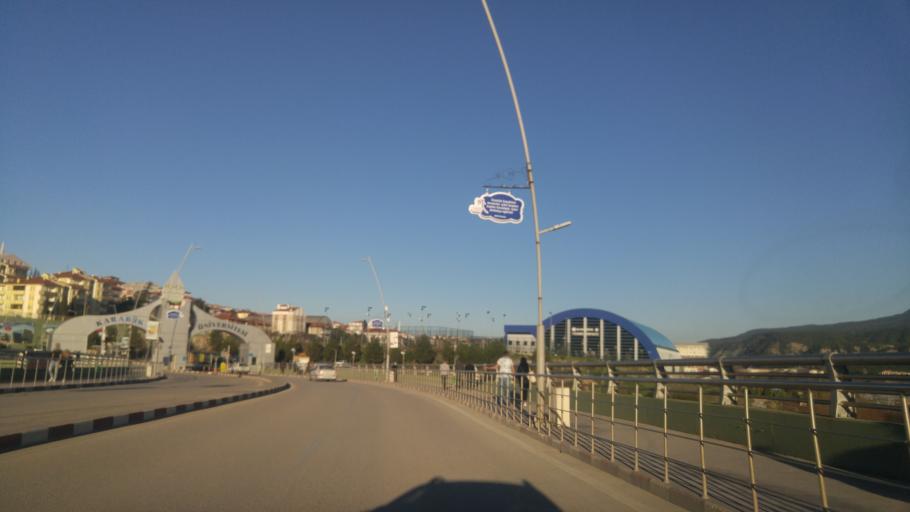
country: TR
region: Karabuk
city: Karabuk
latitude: 41.2154
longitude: 32.6538
